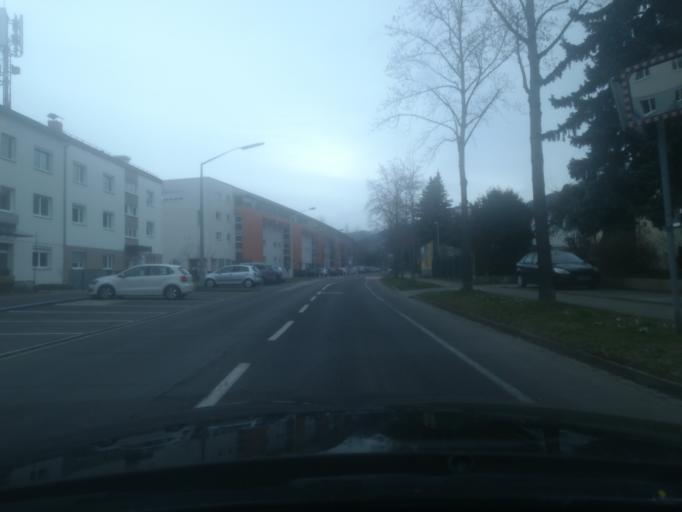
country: AT
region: Upper Austria
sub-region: Linz Stadt
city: Linz
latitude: 48.3299
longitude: 14.3031
